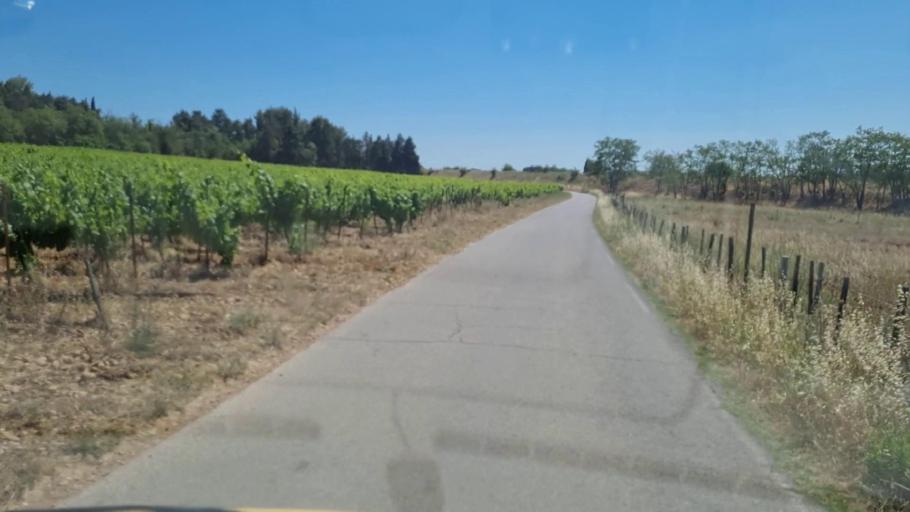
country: FR
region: Languedoc-Roussillon
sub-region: Departement du Gard
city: Le Cailar
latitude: 43.6707
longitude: 4.2627
